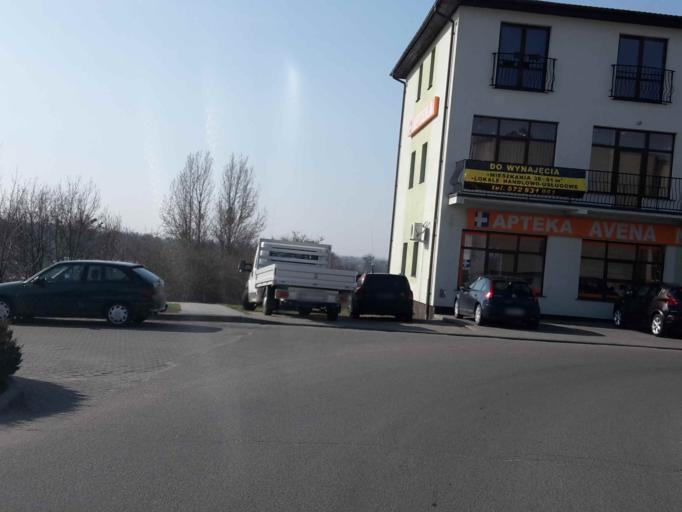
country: PL
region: Kujawsko-Pomorskie
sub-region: Powiat brodnicki
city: Brodnica
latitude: 53.2676
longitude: 19.4102
